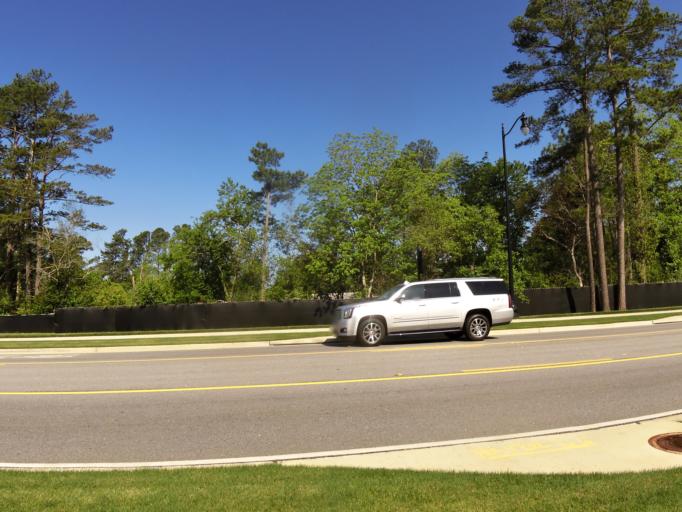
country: US
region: Georgia
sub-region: Columbia County
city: Martinez
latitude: 33.5002
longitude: -82.0308
